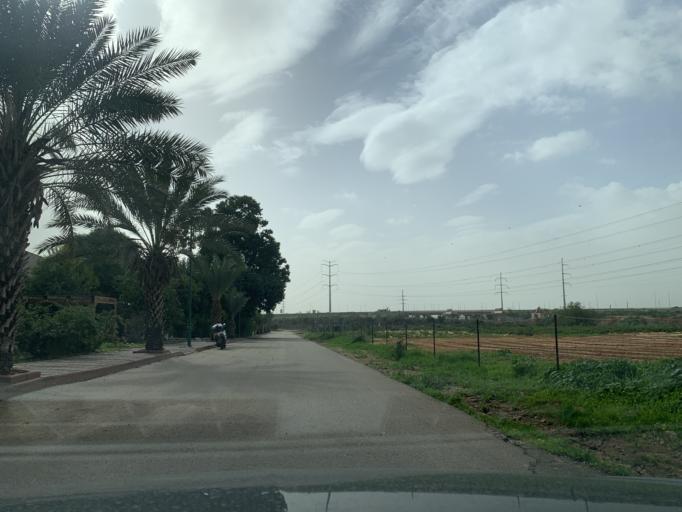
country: IL
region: Central District
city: Jaljulya
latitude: 32.1589
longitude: 34.9390
